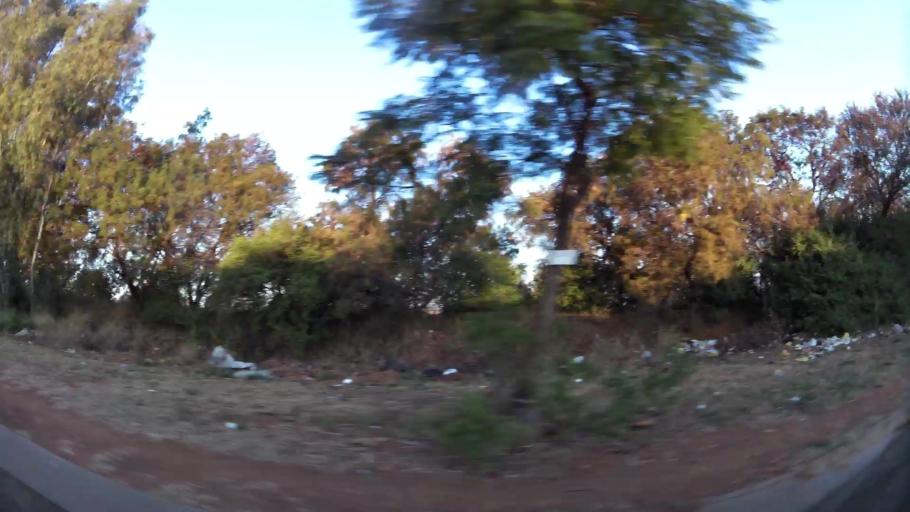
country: ZA
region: Gauteng
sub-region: City of Tshwane Metropolitan Municipality
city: Pretoria
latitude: -25.7407
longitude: 28.1410
